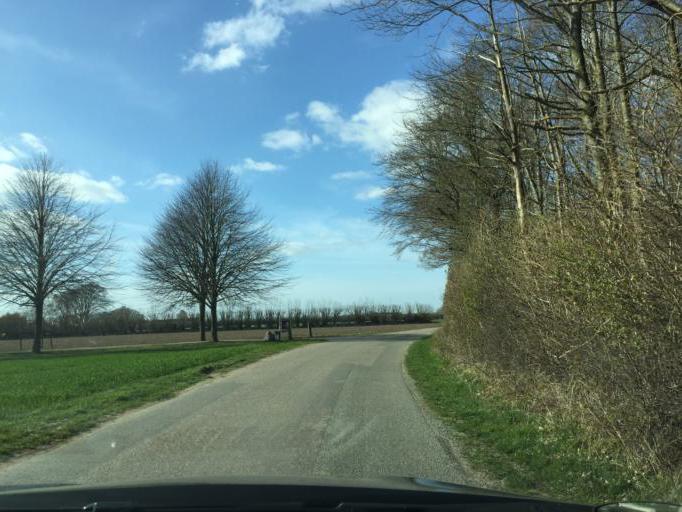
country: DK
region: South Denmark
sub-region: Kerteminde Kommune
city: Langeskov
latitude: 55.3092
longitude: 10.5672
